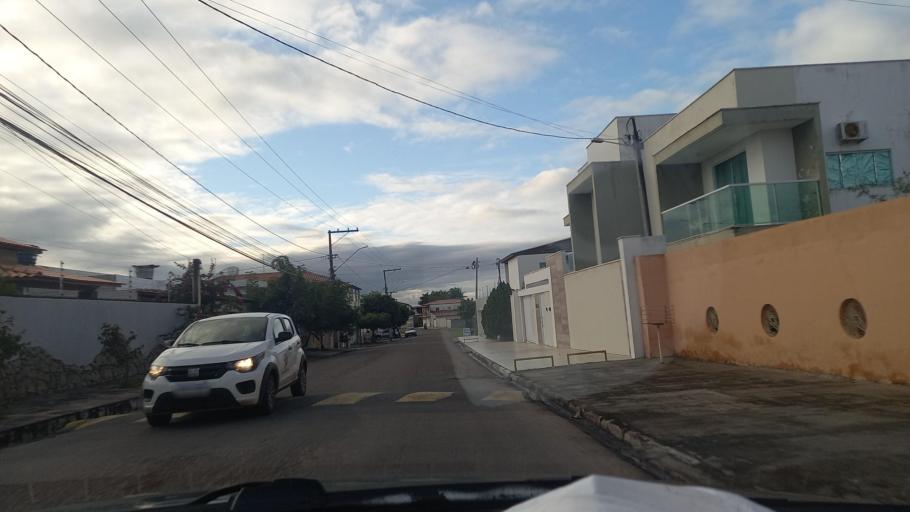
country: BR
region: Bahia
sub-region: Paulo Afonso
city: Paulo Afonso
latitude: -9.3969
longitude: -38.2373
